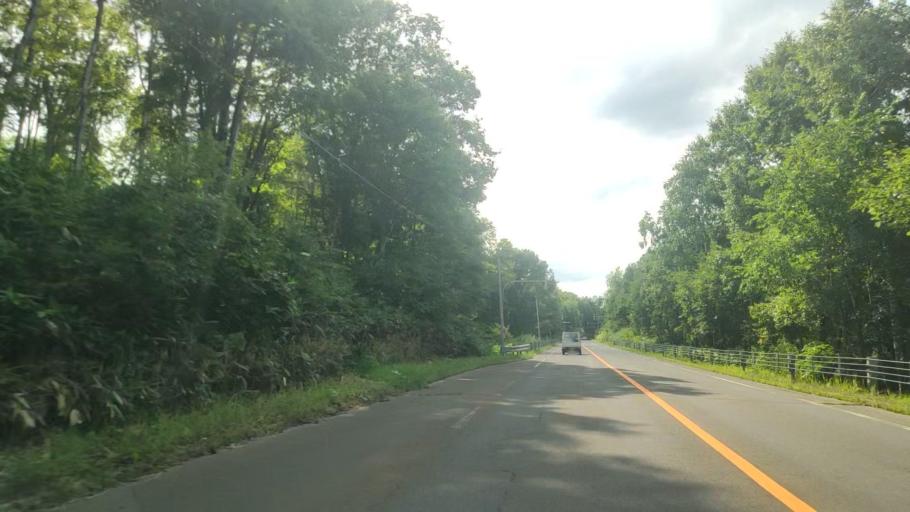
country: JP
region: Hokkaido
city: Nayoro
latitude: 44.3855
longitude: 142.4041
